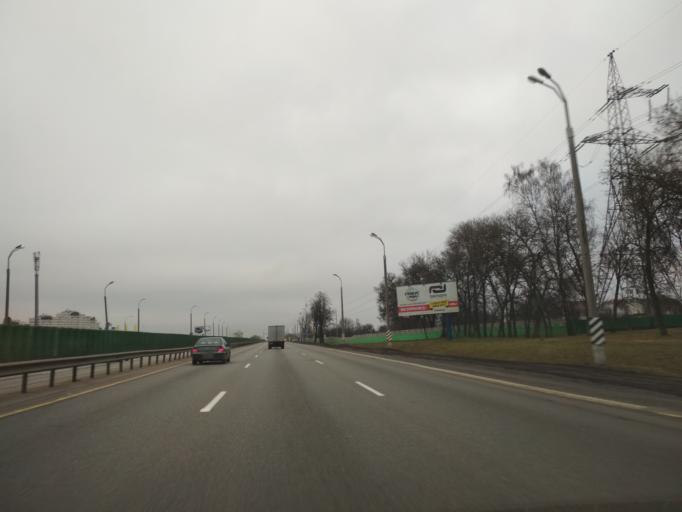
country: BY
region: Minsk
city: Shchomyslitsa
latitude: 53.8433
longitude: 27.4605
